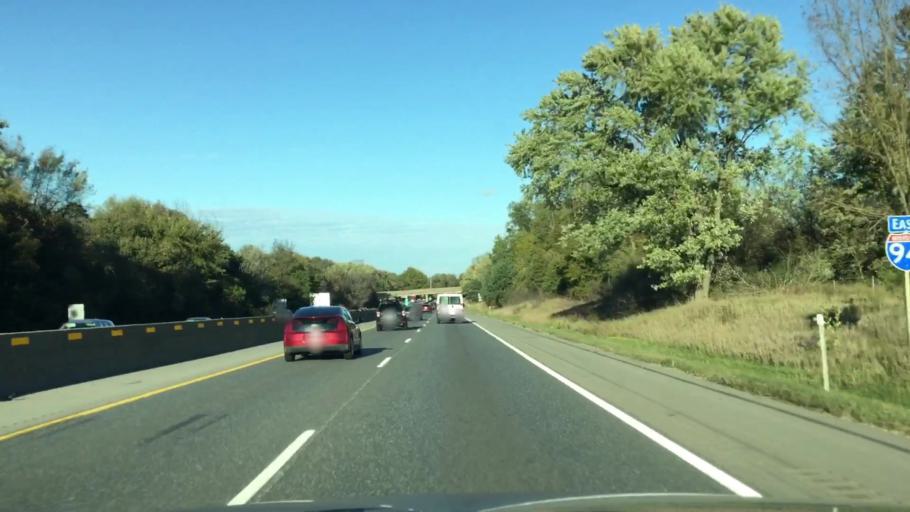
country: US
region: Michigan
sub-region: Kalamazoo County
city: Eastwood
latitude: 42.2639
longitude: -85.5239
